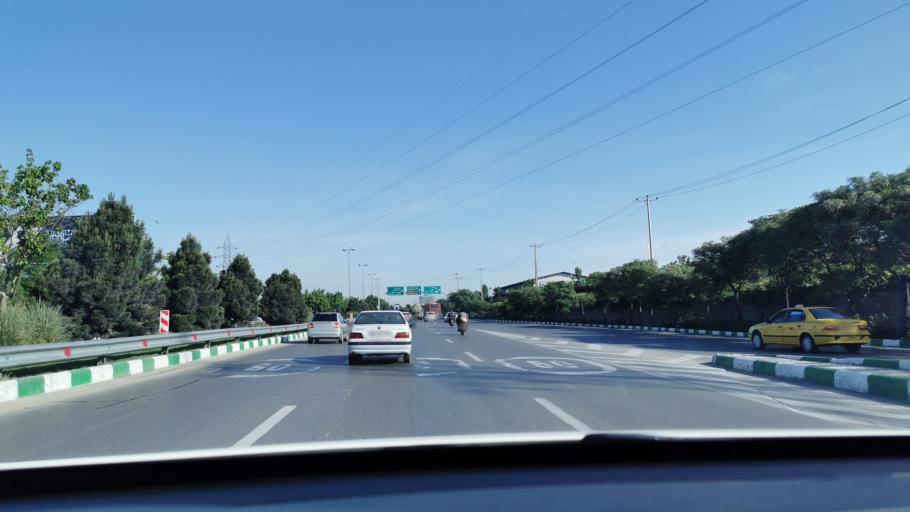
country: IR
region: Razavi Khorasan
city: Mashhad
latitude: 36.2638
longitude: 59.5825
